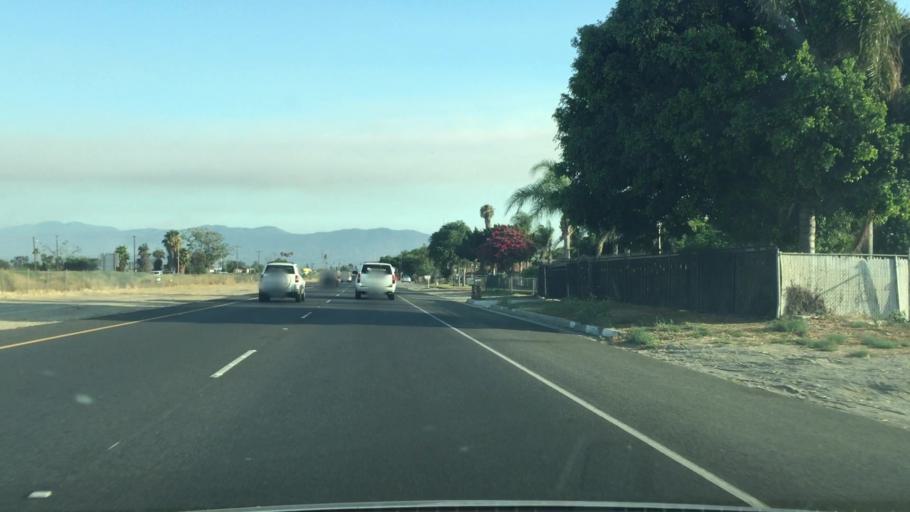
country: US
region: California
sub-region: San Bernardino County
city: Chino
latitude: 34.0172
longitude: -117.6509
